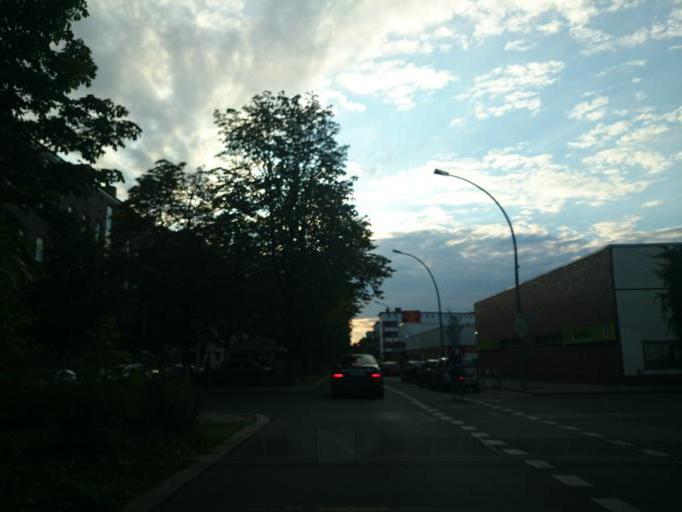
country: DE
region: Berlin
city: Prenzlauer Berg Bezirk
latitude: 52.5408
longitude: 13.4407
